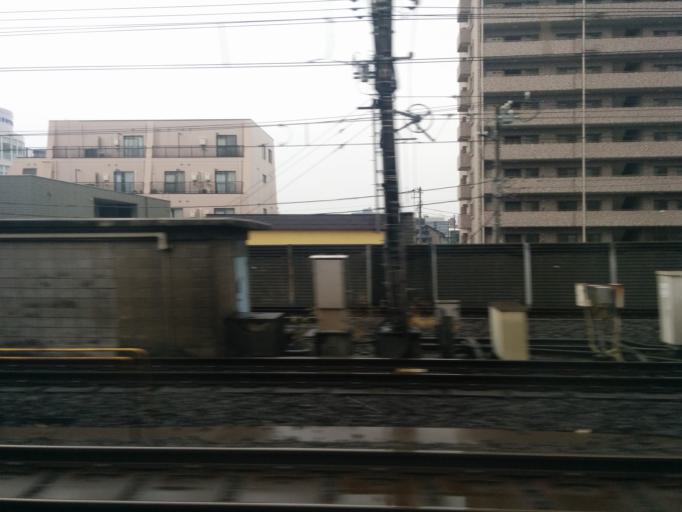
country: JP
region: Chiba
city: Chiba
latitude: 35.6236
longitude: 140.1023
